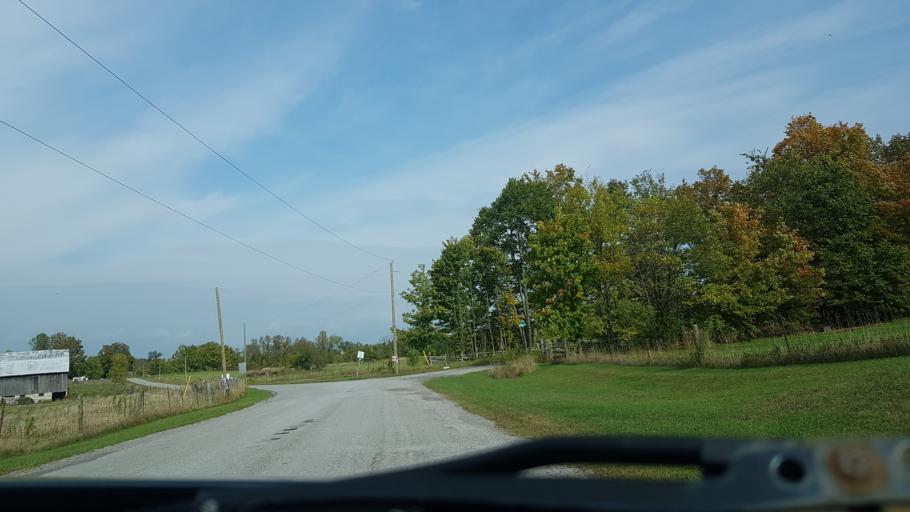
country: CA
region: Ontario
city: Orillia
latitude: 44.6737
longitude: -79.0942
